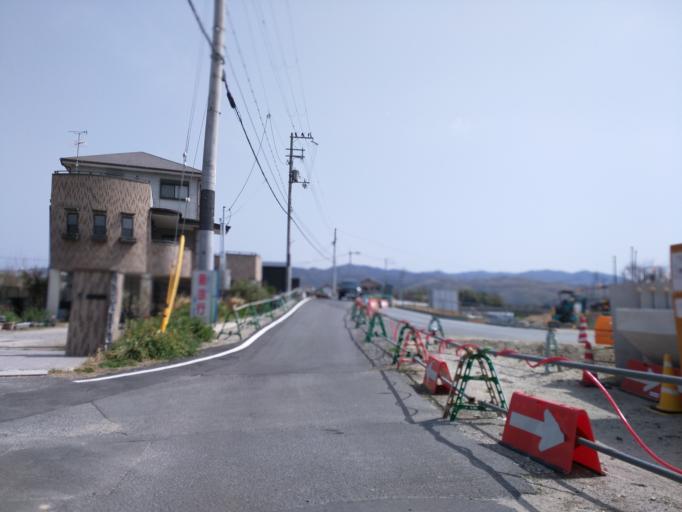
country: JP
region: Kyoto
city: Tanabe
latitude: 34.7814
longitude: 135.7955
